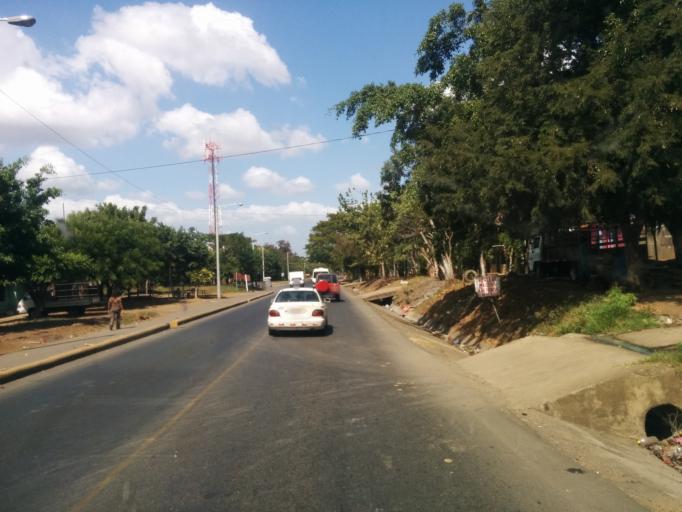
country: NI
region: Masaya
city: Masaya
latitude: 11.9626
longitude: -86.0826
